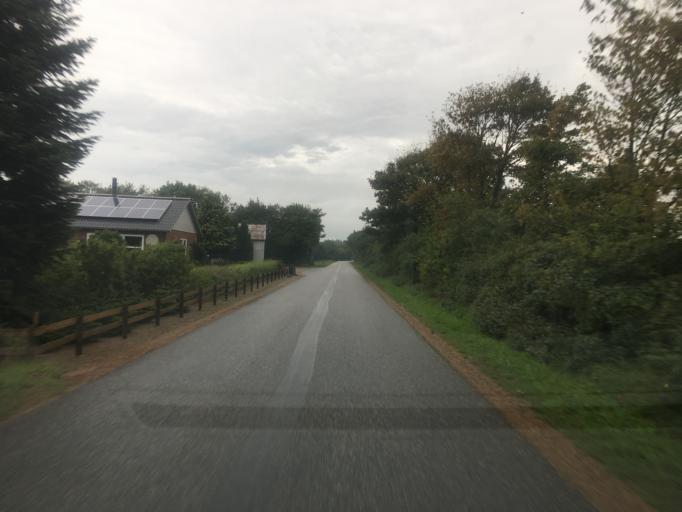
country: DK
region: South Denmark
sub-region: Tonder Kommune
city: Logumkloster
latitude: 55.0132
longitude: 9.0356
